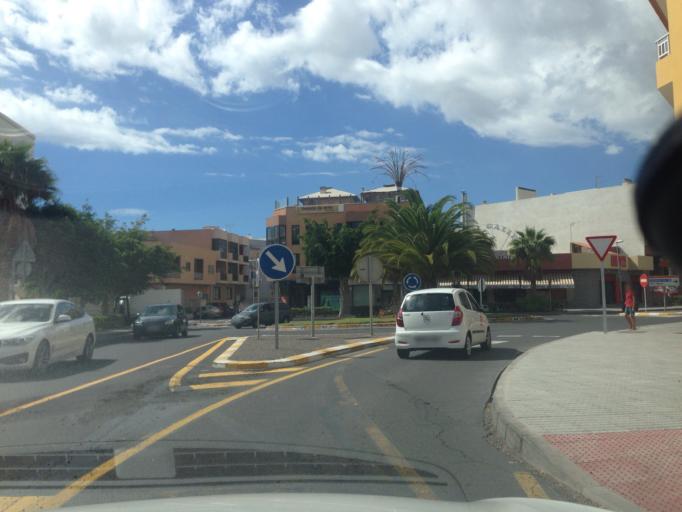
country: ES
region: Canary Islands
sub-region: Provincia de Santa Cruz de Tenerife
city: San Isidro
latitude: 28.0297
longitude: -16.5934
